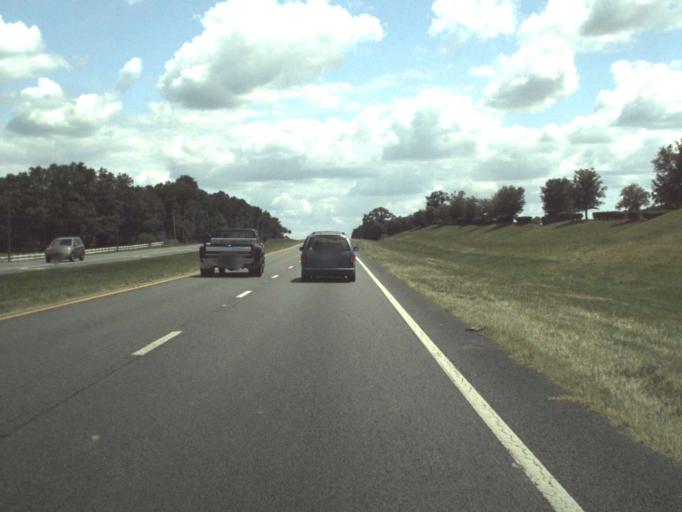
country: US
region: Florida
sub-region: Marion County
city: Ocala
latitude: 29.2811
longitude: -82.1521
